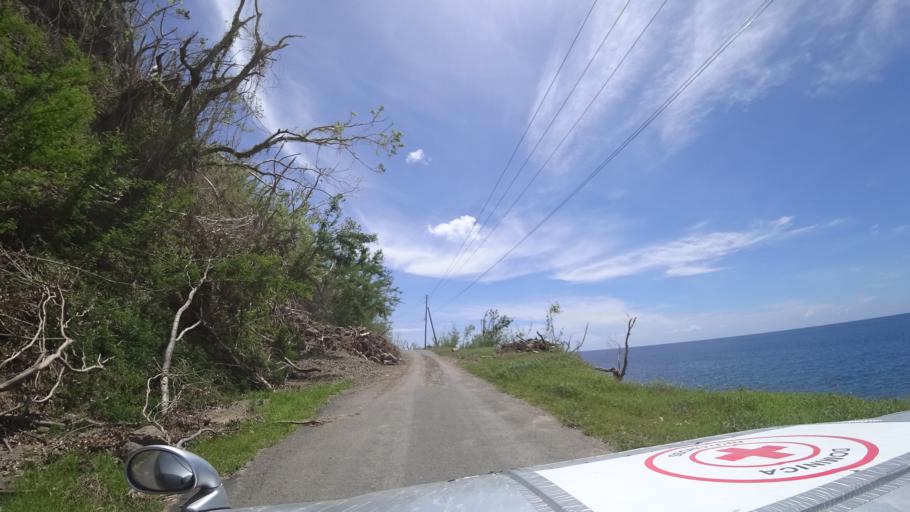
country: DM
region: Saint Luke
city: Pointe Michel
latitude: 15.2530
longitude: -61.3753
